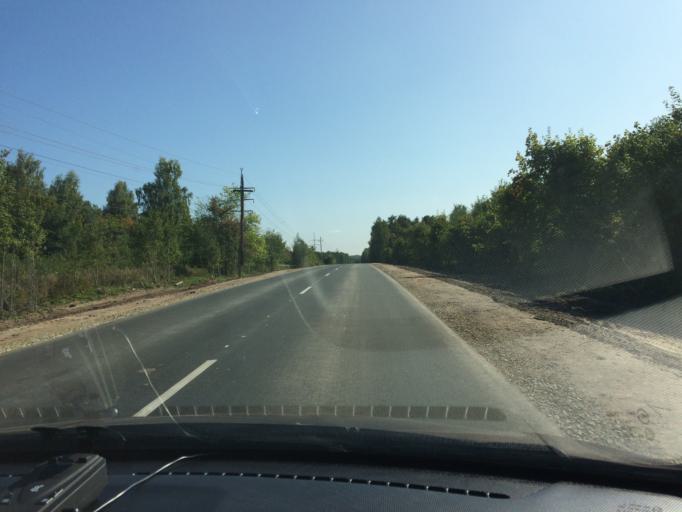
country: RU
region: Mariy-El
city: Sovetskiy
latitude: 56.5459
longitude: 48.4193
